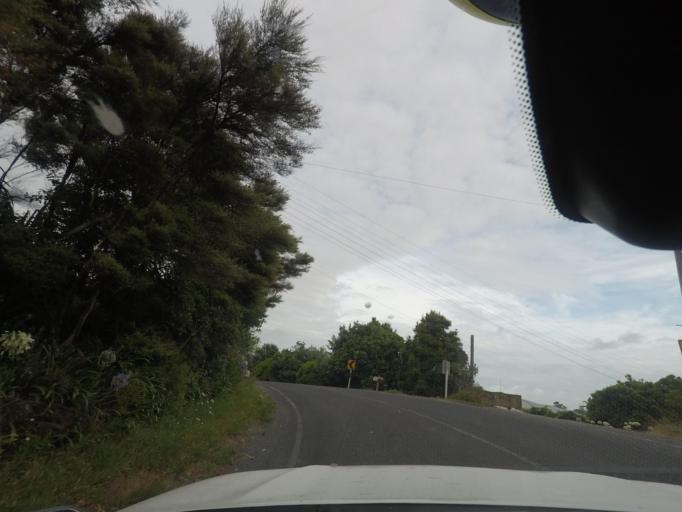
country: NZ
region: Auckland
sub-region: Auckland
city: Parakai
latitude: -36.5276
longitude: 174.2935
